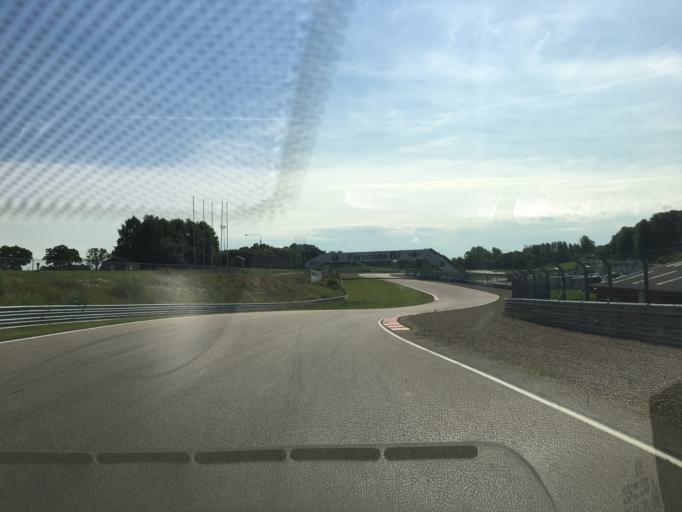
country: SE
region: Skane
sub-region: Svalovs Kommun
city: Kagerod
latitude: 55.9891
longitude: 13.1114
